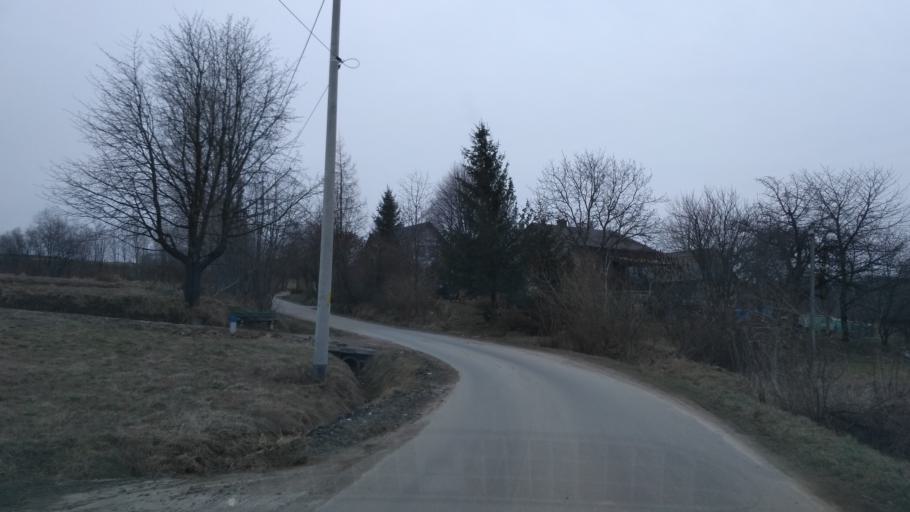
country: PL
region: Subcarpathian Voivodeship
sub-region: Powiat rzeszowski
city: Siedliska
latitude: 49.9294
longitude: 21.9613
